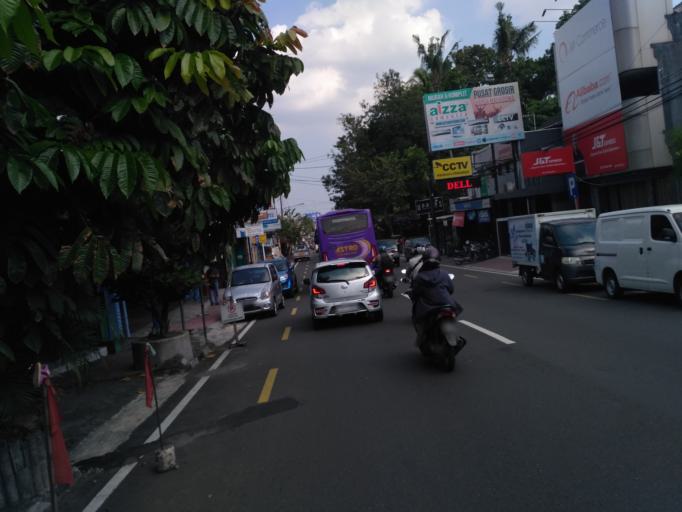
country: ID
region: Daerah Istimewa Yogyakarta
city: Yogyakarta
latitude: -7.7588
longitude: 110.3697
